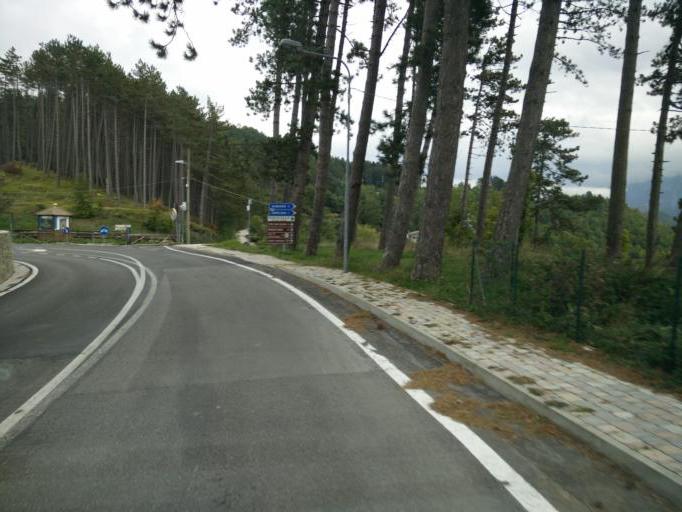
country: IT
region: Tuscany
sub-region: Provincia di Lucca
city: Giuncugnano
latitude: 44.2006
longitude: 10.2309
